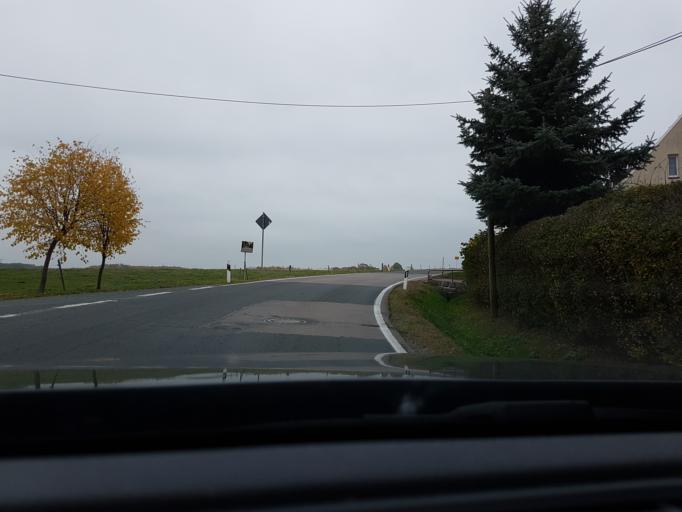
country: DE
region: Saxony
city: Altmittweida
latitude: 50.9825
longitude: 12.9353
